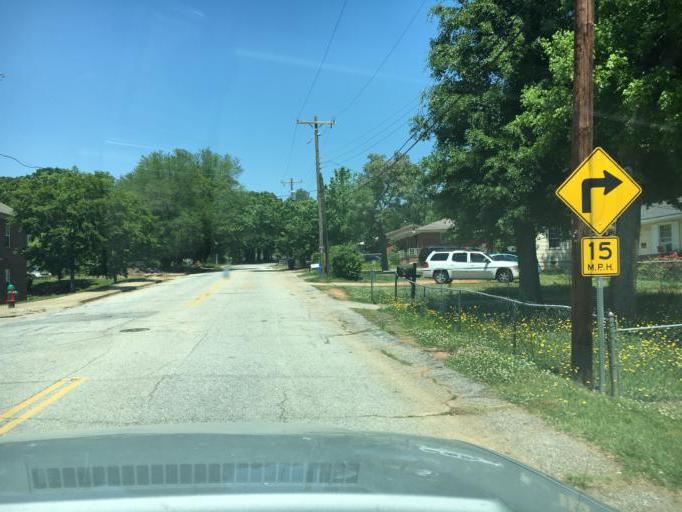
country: US
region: South Carolina
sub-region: Spartanburg County
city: Spartanburg
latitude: 34.9461
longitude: -81.9505
